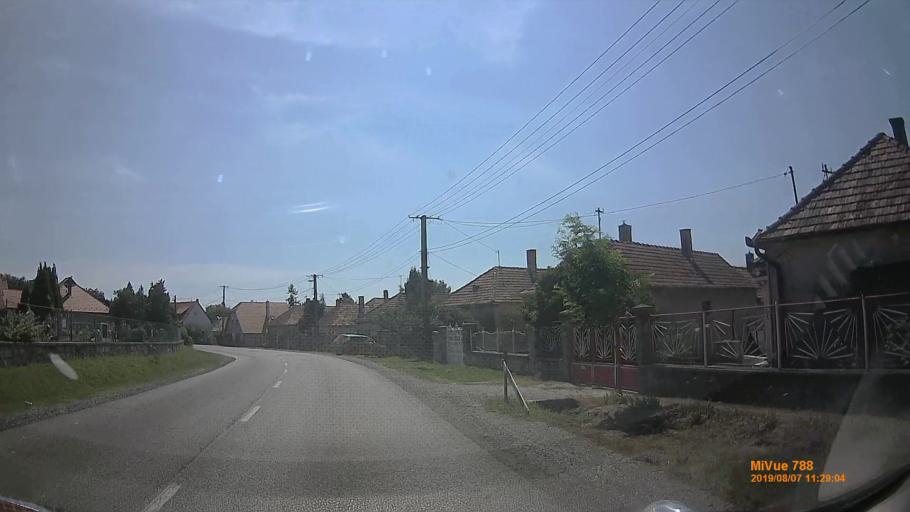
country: HU
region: Veszprem
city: Tapolca
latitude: 46.9174
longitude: 17.4531
